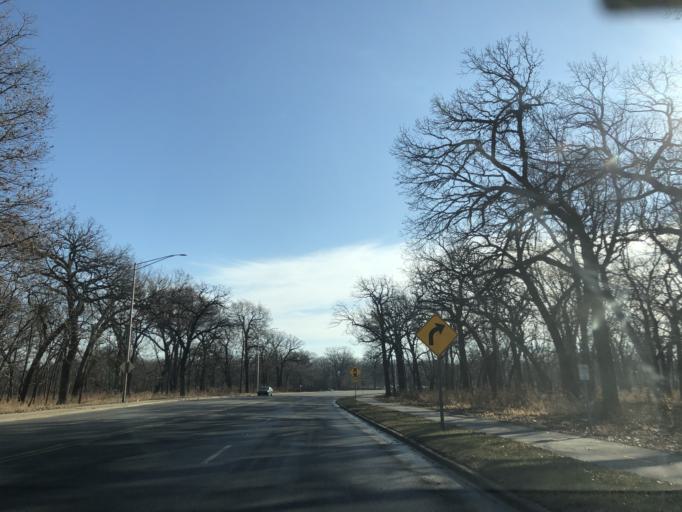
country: US
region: Illinois
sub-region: Cook County
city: Riverside
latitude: 41.8372
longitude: -87.8316
